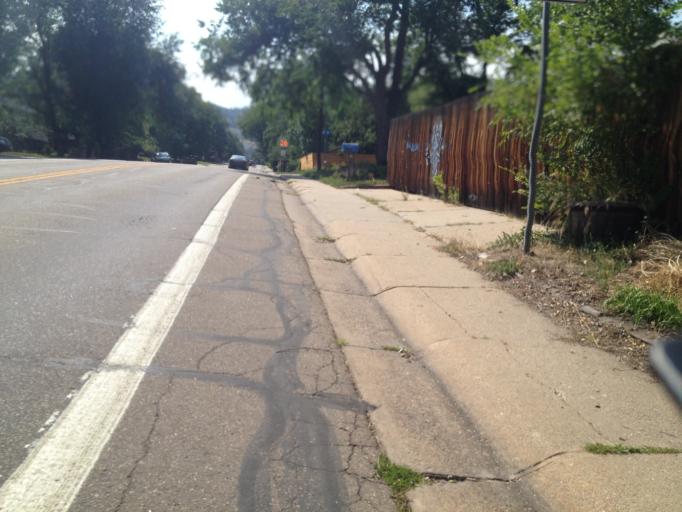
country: US
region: Colorado
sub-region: Boulder County
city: Boulder
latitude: 40.0268
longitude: -105.2732
